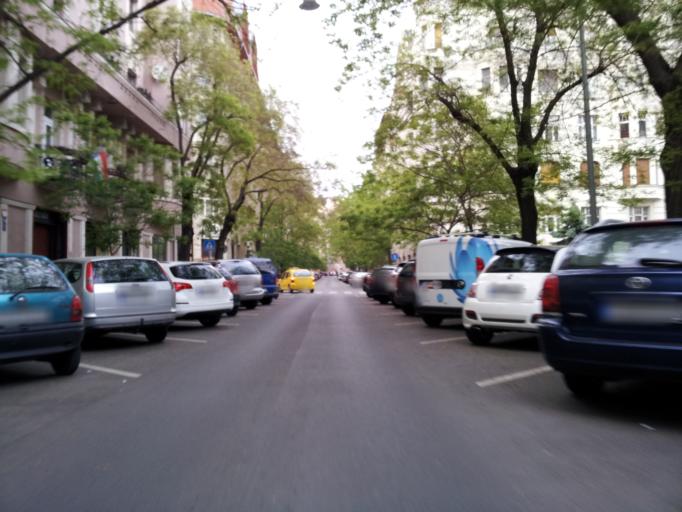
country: HU
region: Budapest
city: Budapest
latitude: 47.5104
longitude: 19.0484
